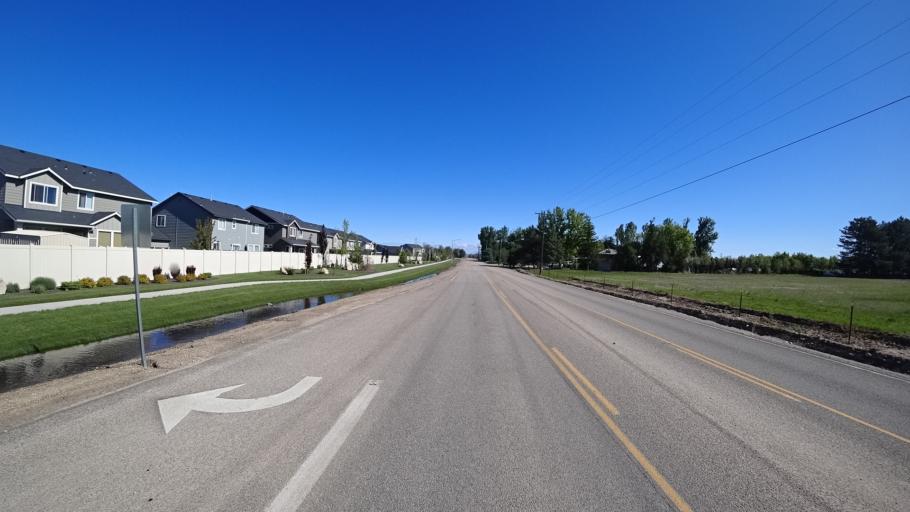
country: US
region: Idaho
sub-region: Ada County
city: Star
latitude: 43.6506
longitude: -116.4537
